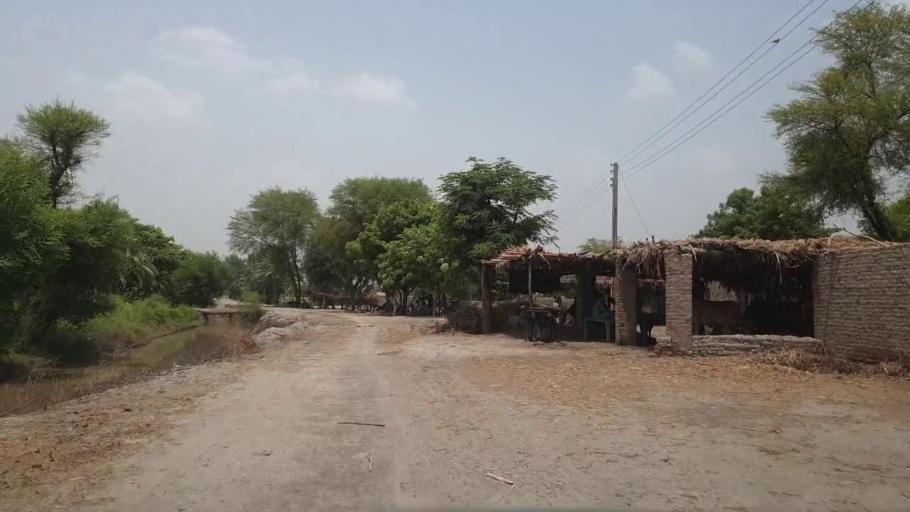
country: PK
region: Sindh
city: Sobhadero
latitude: 27.4361
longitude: 68.4088
